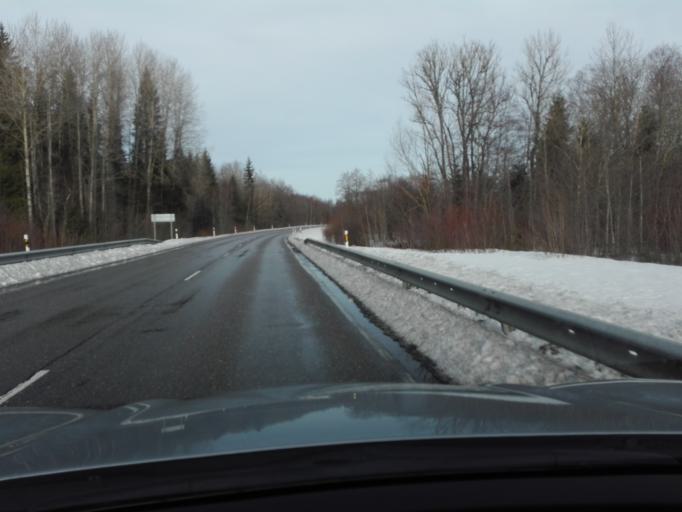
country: EE
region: Raplamaa
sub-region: Rapla vald
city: Rapla
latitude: 58.9690
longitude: 24.7666
